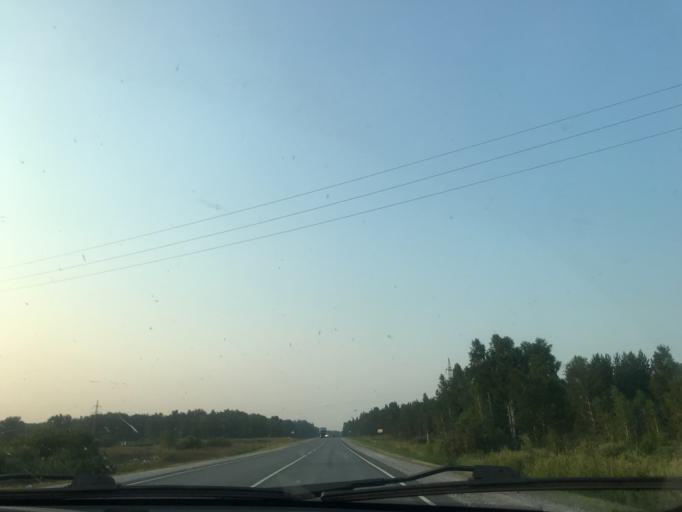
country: RU
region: Novosibirsk
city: Dorogino
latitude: 54.3752
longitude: 83.3054
